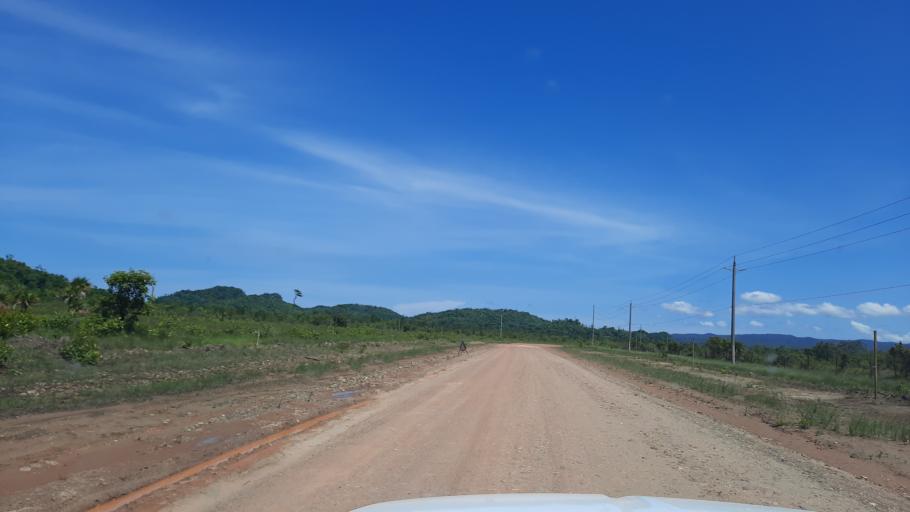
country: BZ
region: Stann Creek
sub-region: Dangriga
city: Dangriga
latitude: 17.1971
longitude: -88.3997
